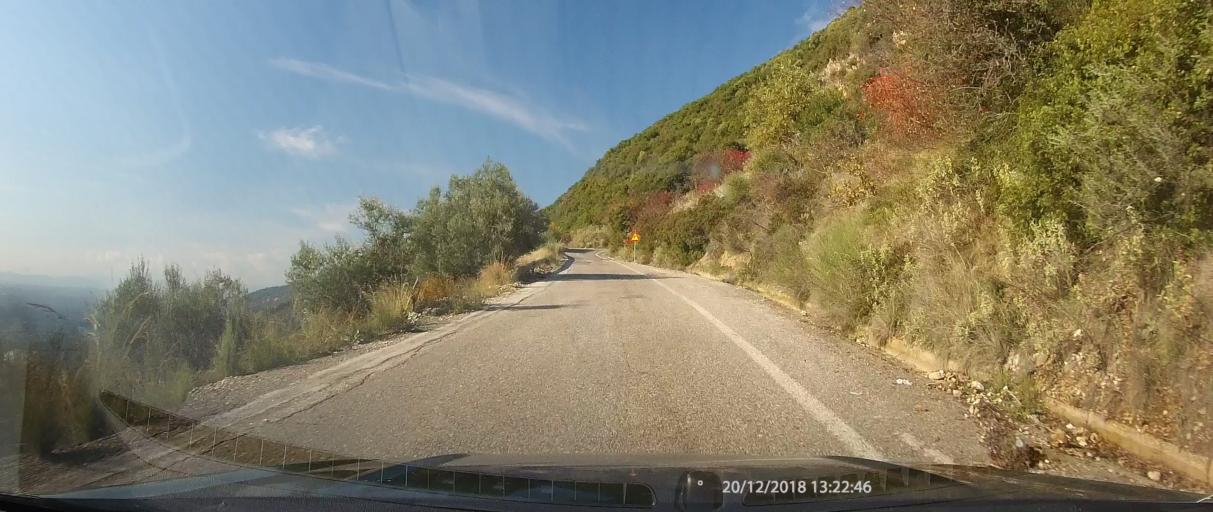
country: GR
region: West Greece
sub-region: Nomos Aitolias kai Akarnanias
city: Paravola
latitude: 38.6168
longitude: 21.5630
